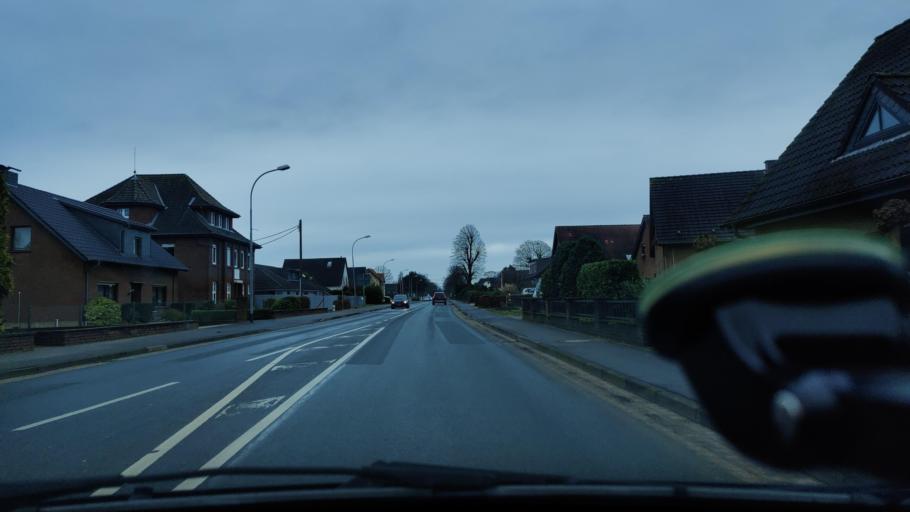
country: DE
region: North Rhine-Westphalia
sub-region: Regierungsbezirk Dusseldorf
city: Alpen
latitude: 51.5760
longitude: 6.4718
